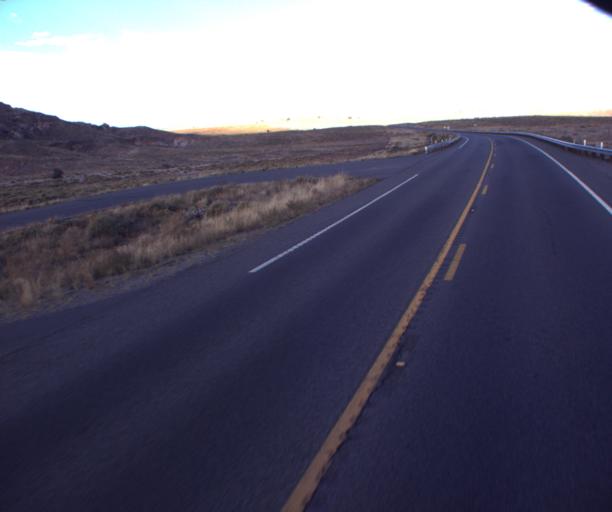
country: US
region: New Mexico
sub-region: San Juan County
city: Shiprock
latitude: 36.9355
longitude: -109.1142
